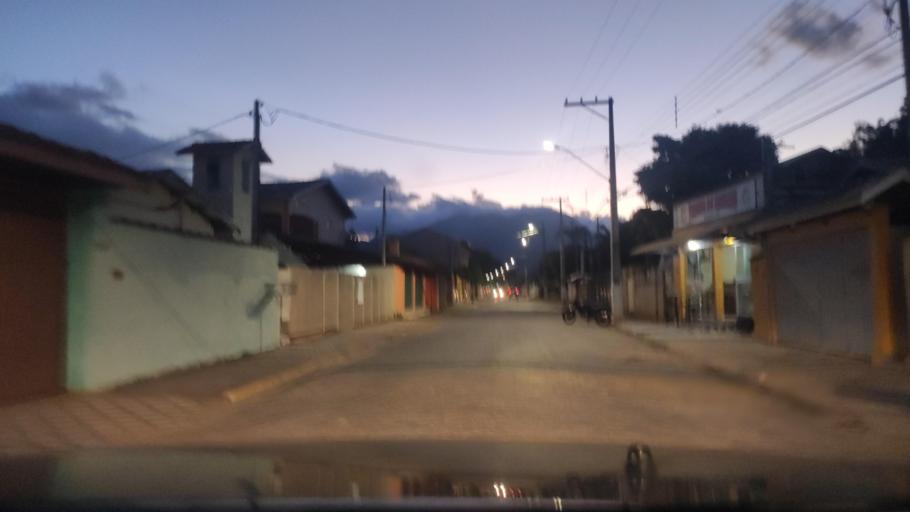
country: BR
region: Minas Gerais
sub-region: Paraisopolis
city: Paraisopolis
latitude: -22.6917
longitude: -45.7403
